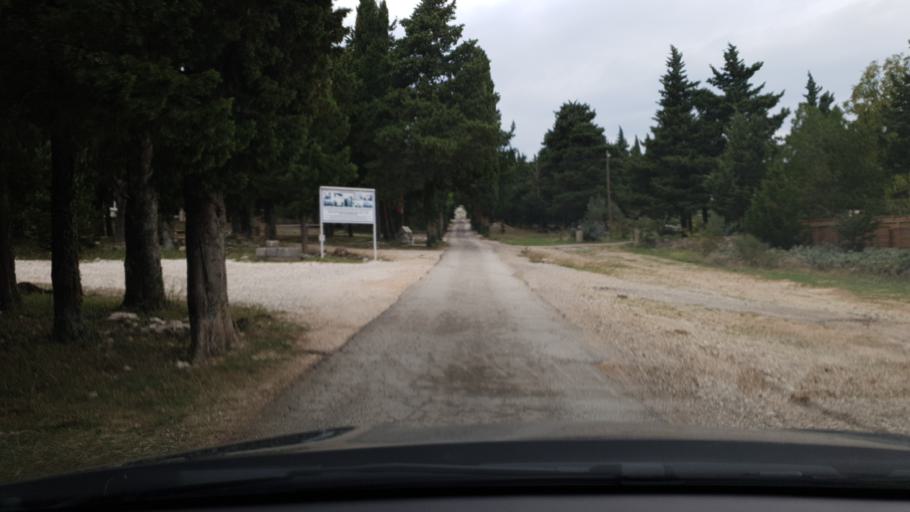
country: HR
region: Dubrovacko-Neretvanska
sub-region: Grad Dubrovnik
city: Dubrovnik
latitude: 42.6433
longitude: 18.1267
